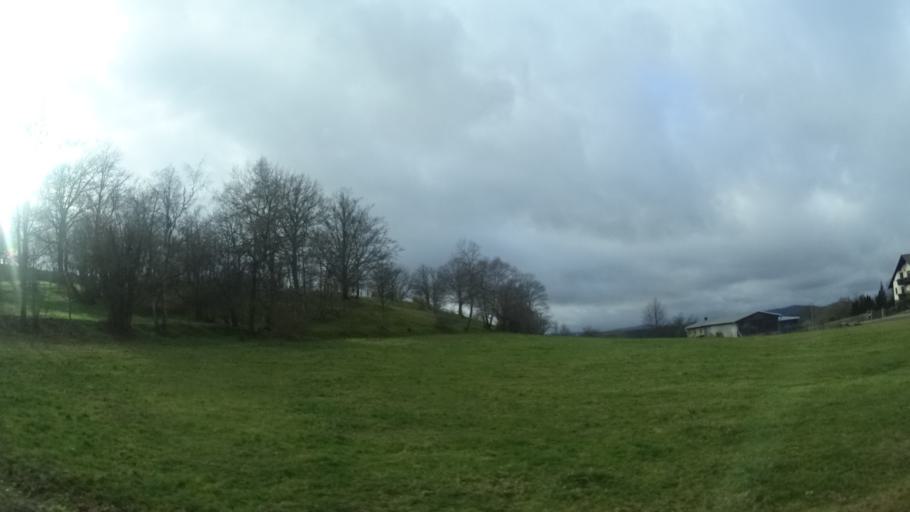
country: DE
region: Thuringia
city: Doschnitz
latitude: 50.6136
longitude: 11.2970
